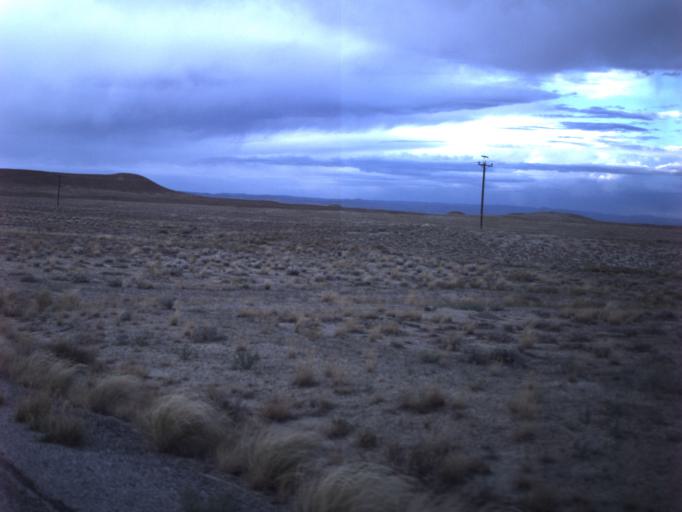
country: US
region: Utah
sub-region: Grand County
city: Moab
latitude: 38.9216
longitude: -109.3354
